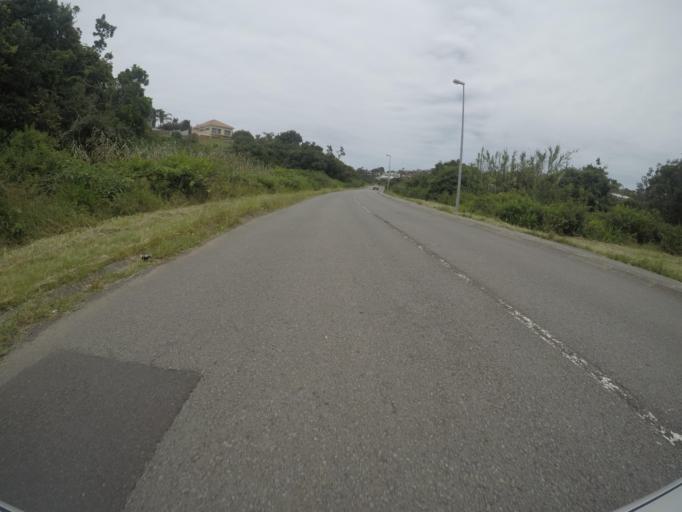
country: ZA
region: Eastern Cape
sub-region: Buffalo City Metropolitan Municipality
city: East London
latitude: -32.9787
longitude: 27.9334
